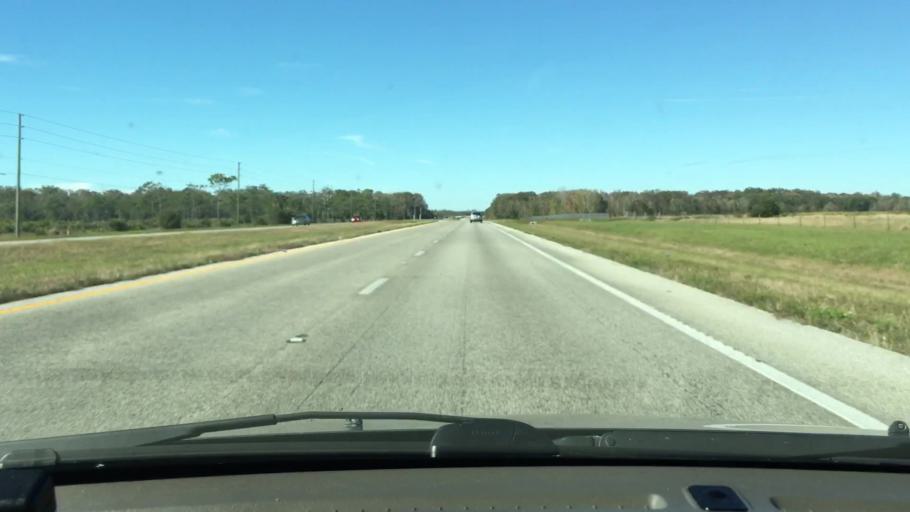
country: US
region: Florida
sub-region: Osceola County
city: Saint Cloud
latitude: 28.1295
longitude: -80.9942
